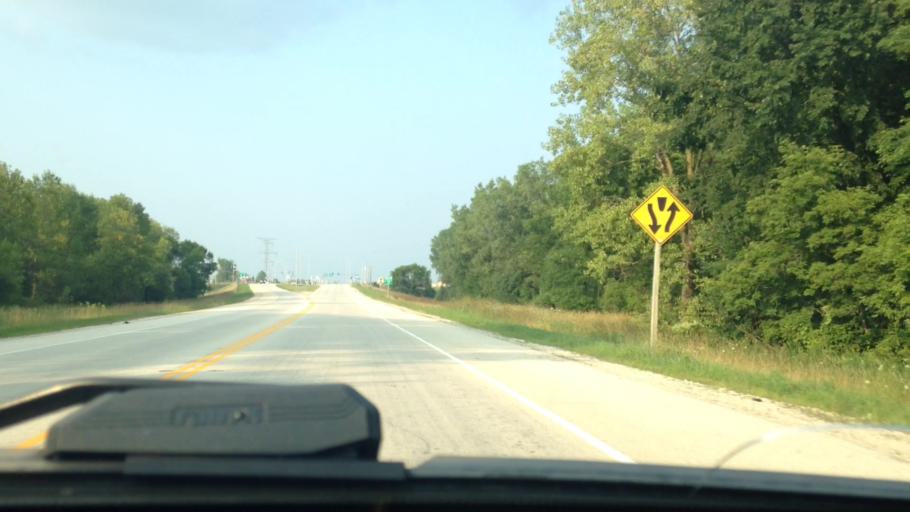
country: US
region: Wisconsin
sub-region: Washington County
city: Germantown
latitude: 43.2102
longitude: -88.1545
